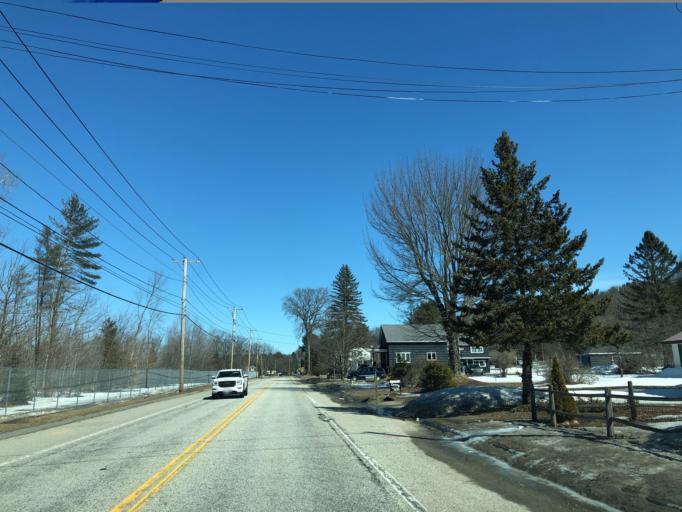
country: US
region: Maine
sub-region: Androscoggin County
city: Minot
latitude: 44.0482
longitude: -70.2768
